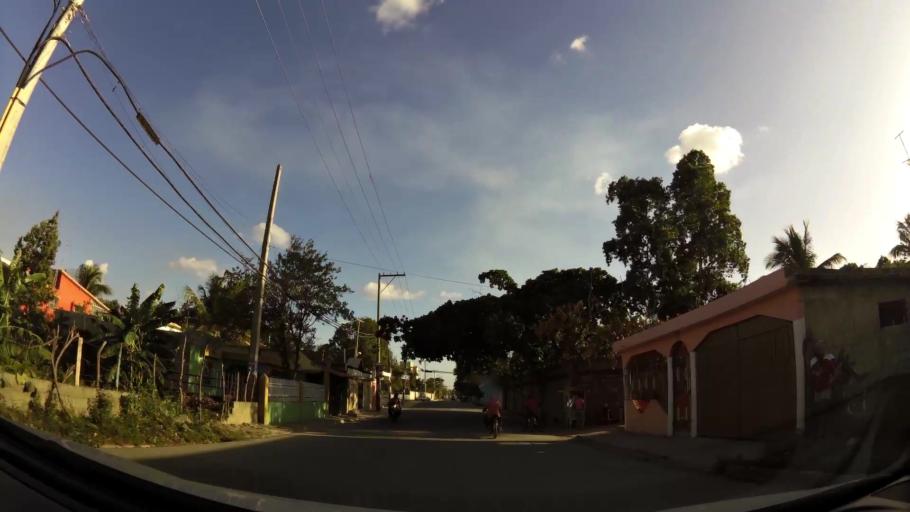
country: DO
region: Santo Domingo
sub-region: Santo Domingo
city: Santo Domingo Este
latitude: 18.4728
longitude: -69.7946
